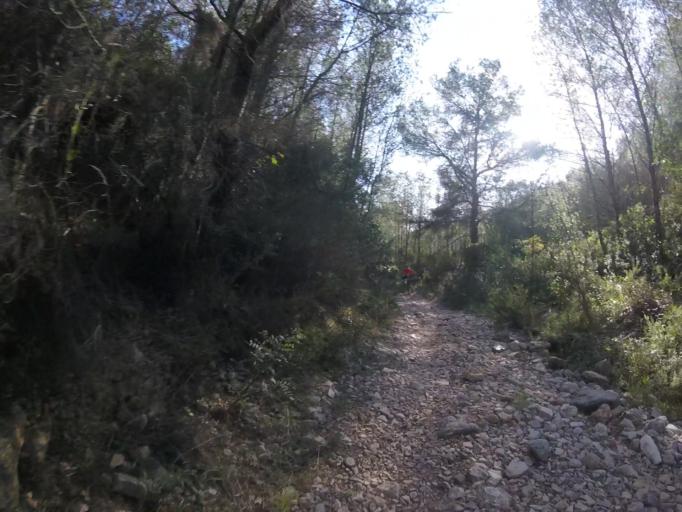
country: ES
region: Valencia
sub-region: Provincia de Castello
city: Santa Magdalena de Pulpis
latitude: 40.3089
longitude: 0.3340
